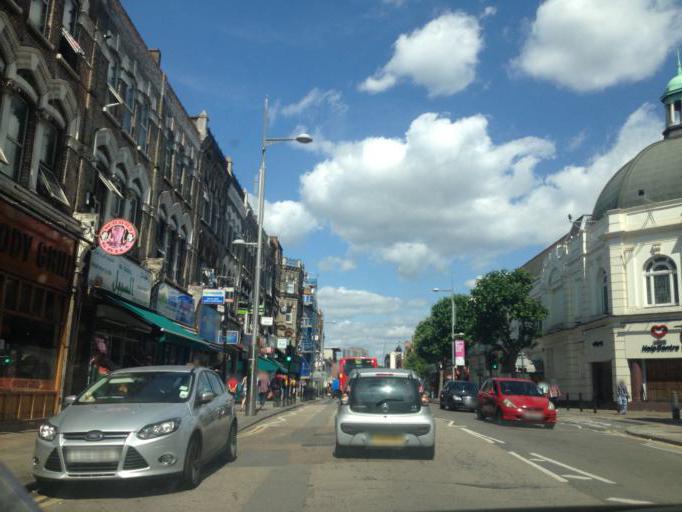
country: GB
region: England
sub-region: Greater London
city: Belsize Park
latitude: 51.5420
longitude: -0.1982
